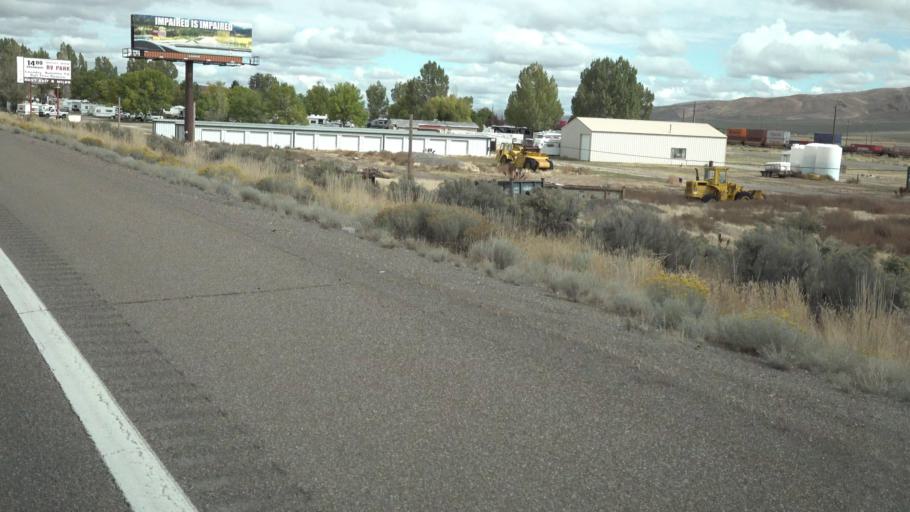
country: US
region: Nevada
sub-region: Elko County
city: Elko
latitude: 40.8852
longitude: -115.7142
